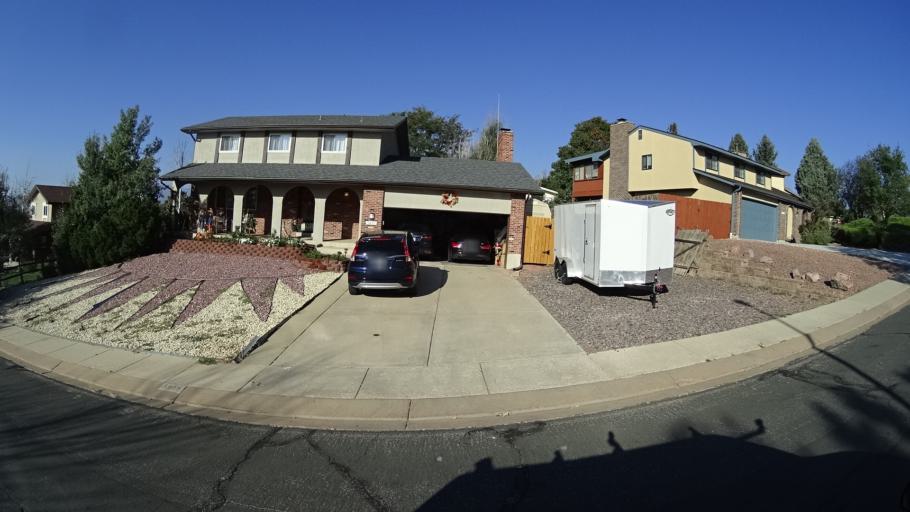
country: US
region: Colorado
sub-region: El Paso County
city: Cimarron Hills
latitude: 38.8877
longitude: -104.7270
